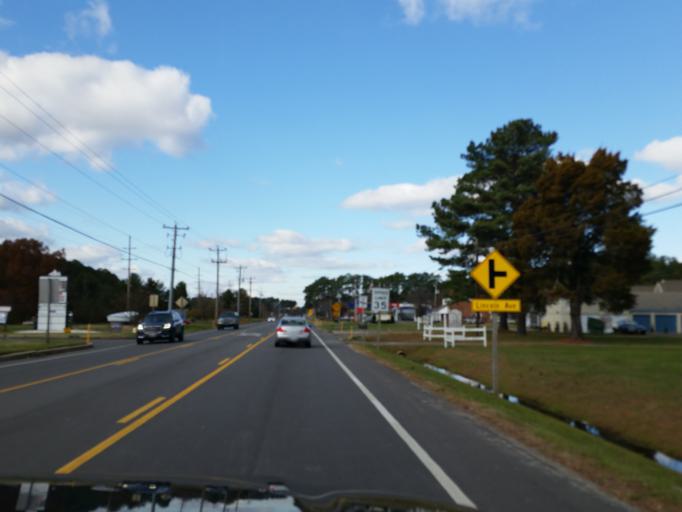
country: US
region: Maryland
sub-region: Talbot County
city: Saint Michaels
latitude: 38.7725
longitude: -76.2103
